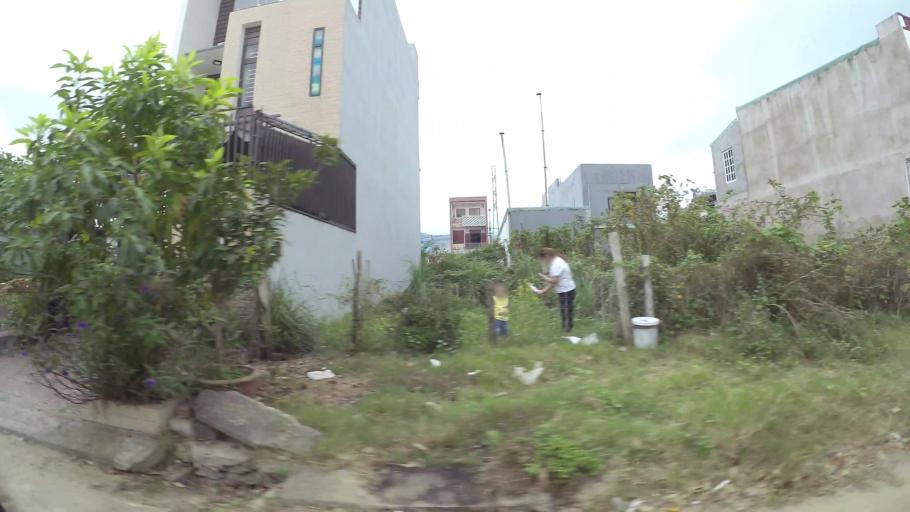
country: VN
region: Da Nang
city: Lien Chieu
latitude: 16.0505
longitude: 108.1680
